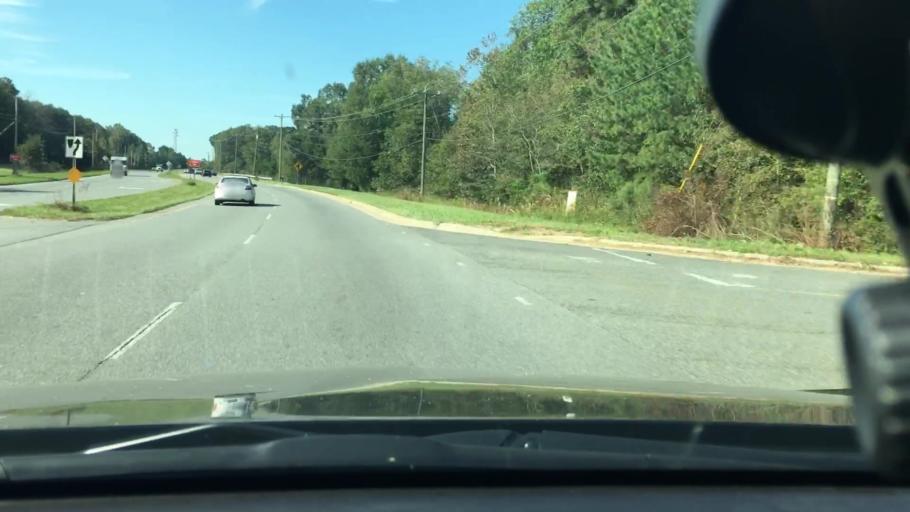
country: US
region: North Carolina
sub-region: Mecklenburg County
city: Mint Hill
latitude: 35.2321
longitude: -80.6045
